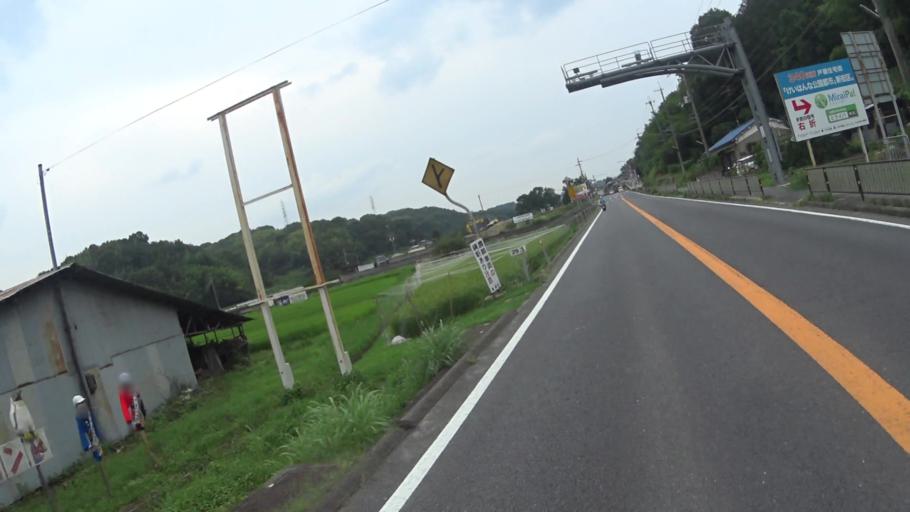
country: JP
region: Nara
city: Nara-shi
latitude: 34.7305
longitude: 135.7665
